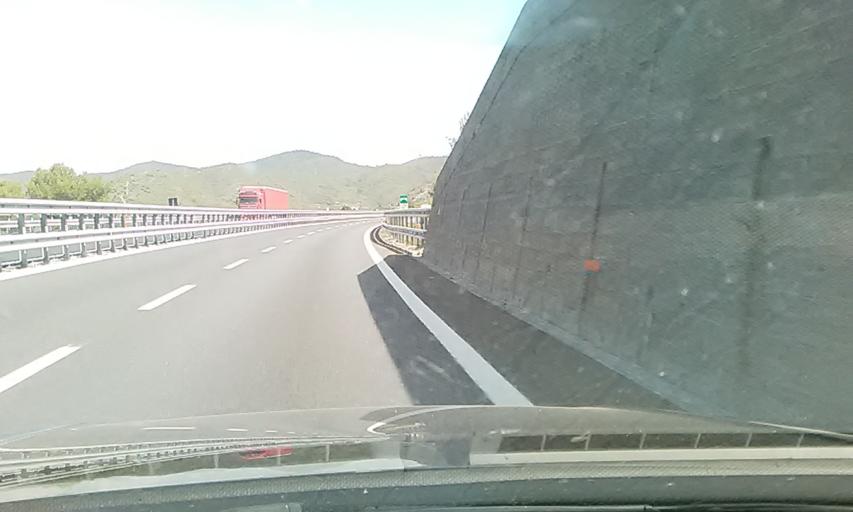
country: IT
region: Liguria
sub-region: Provincia di Savona
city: Laigueglia
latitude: 43.9840
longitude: 8.1365
